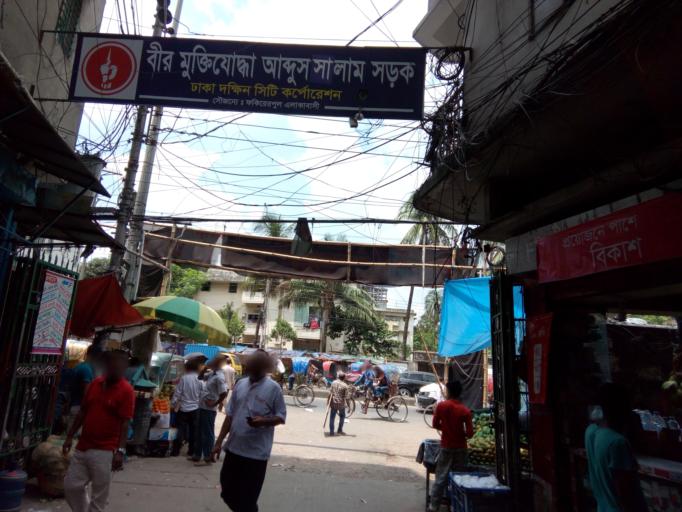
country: BD
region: Dhaka
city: Paltan
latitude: 23.7341
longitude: 90.4180
